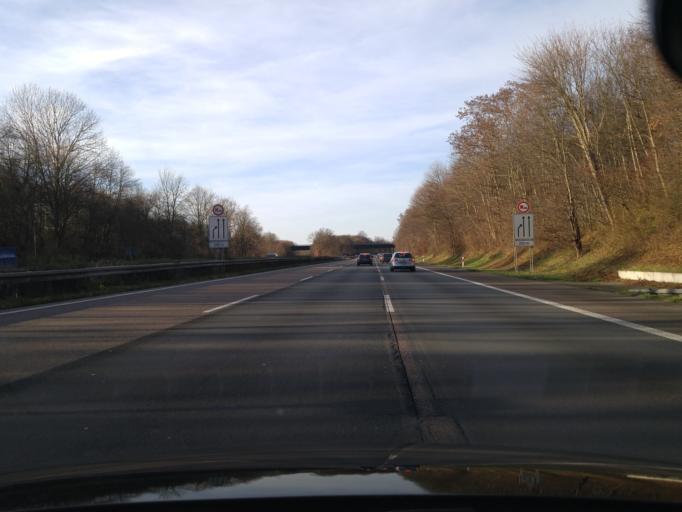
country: DE
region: North Rhine-Westphalia
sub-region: Regierungsbezirk Koln
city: Gremberghoven
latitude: 50.9206
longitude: 7.0705
